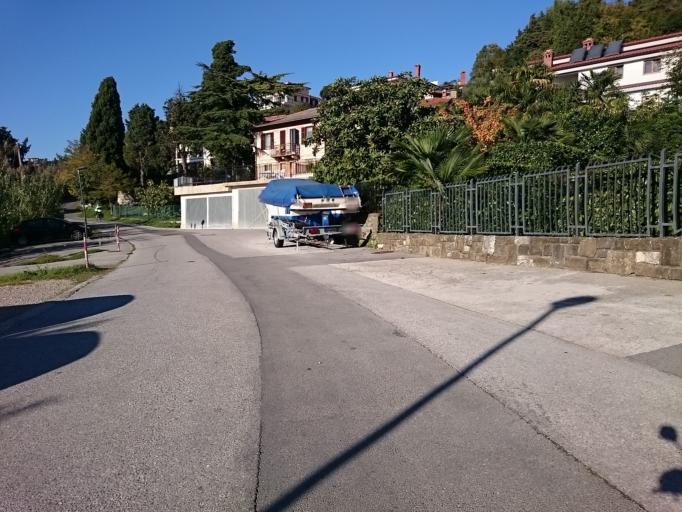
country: SI
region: Piran-Pirano
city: Portoroz
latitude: 45.5120
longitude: 13.5976
